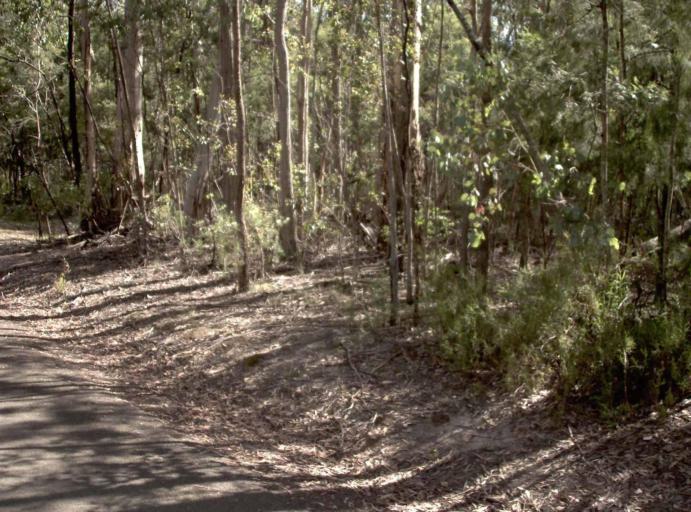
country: AU
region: Victoria
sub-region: East Gippsland
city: Lakes Entrance
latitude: -37.4724
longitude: 148.1239
